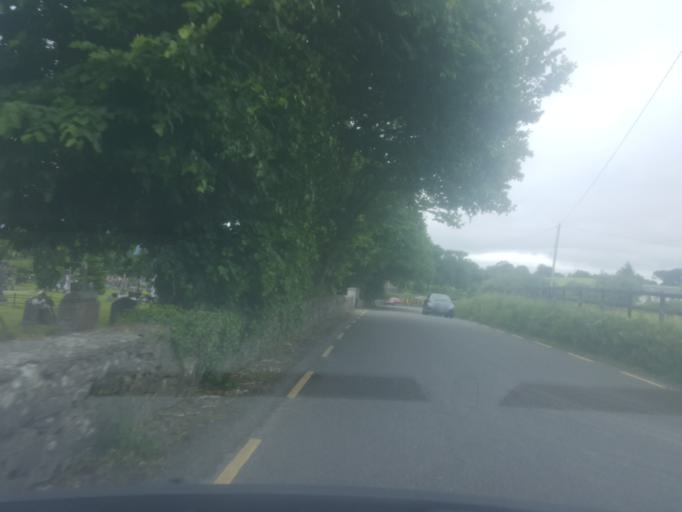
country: IE
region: Munster
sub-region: Ciarrai
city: Cill Airne
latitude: 52.0784
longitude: -9.5097
